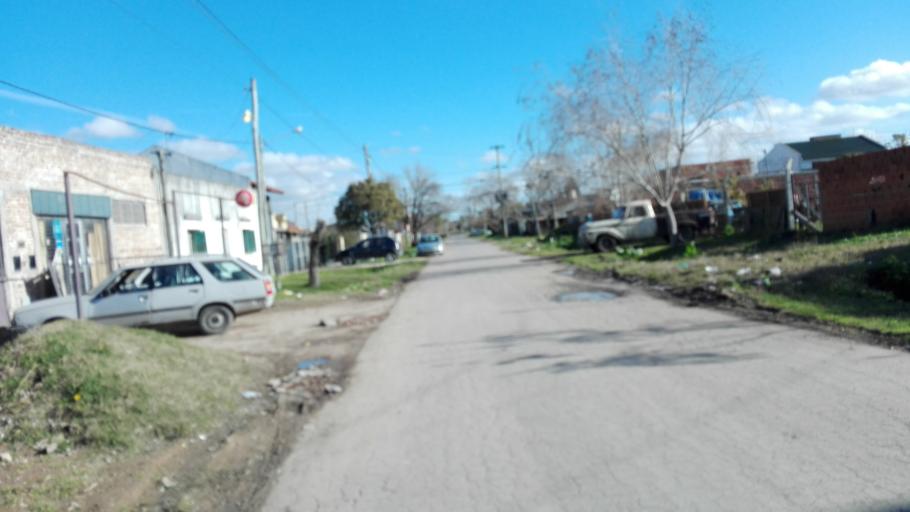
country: AR
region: Buenos Aires
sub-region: Partido de La Plata
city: La Plata
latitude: -34.8780
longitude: -57.9956
